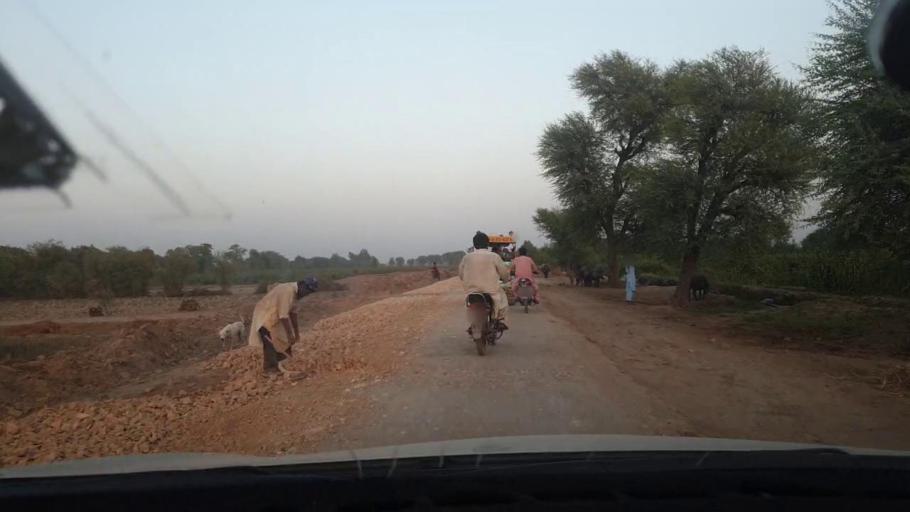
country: PK
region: Sindh
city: Bhit Shah
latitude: 25.7527
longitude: 68.5124
